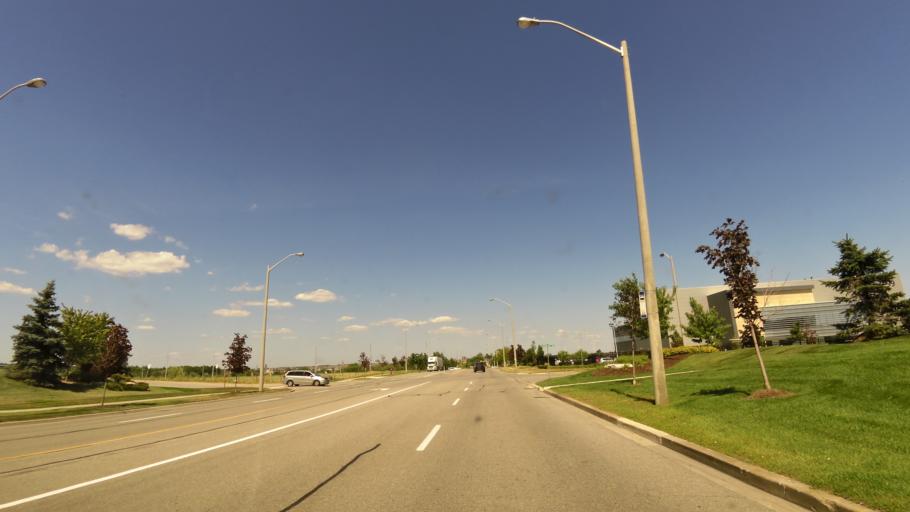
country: CA
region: Ontario
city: Brampton
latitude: 43.6209
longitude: -79.7731
